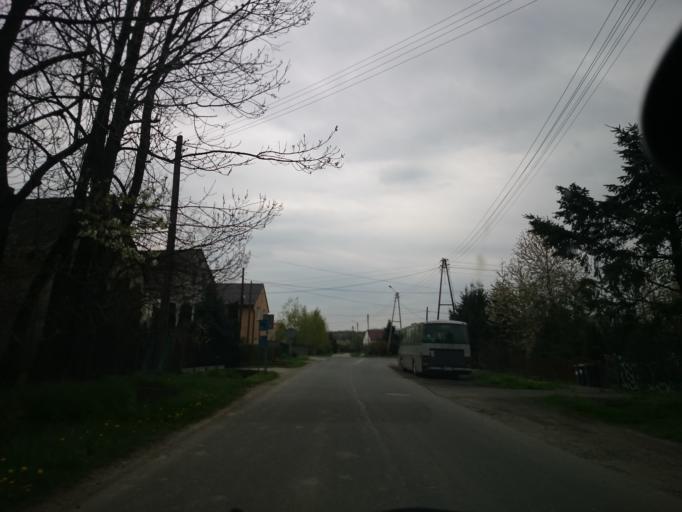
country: PL
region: Opole Voivodeship
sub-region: Powiat nyski
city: Glucholazy
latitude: 50.3205
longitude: 17.4323
